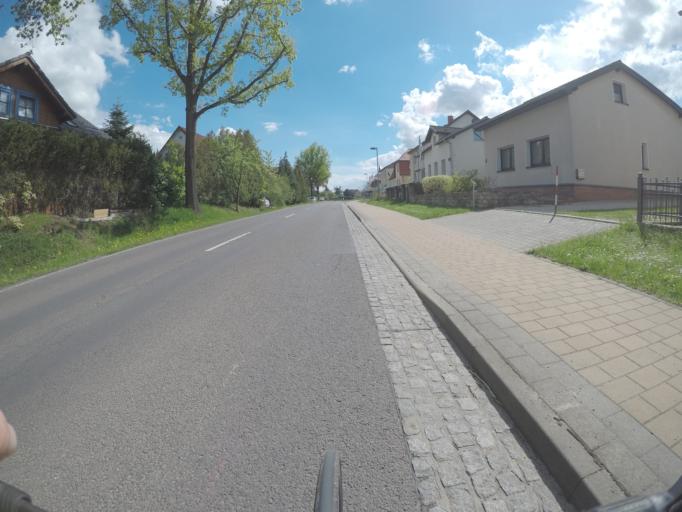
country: DE
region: Brandenburg
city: Bernau bei Berlin
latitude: 52.6905
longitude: 13.5883
